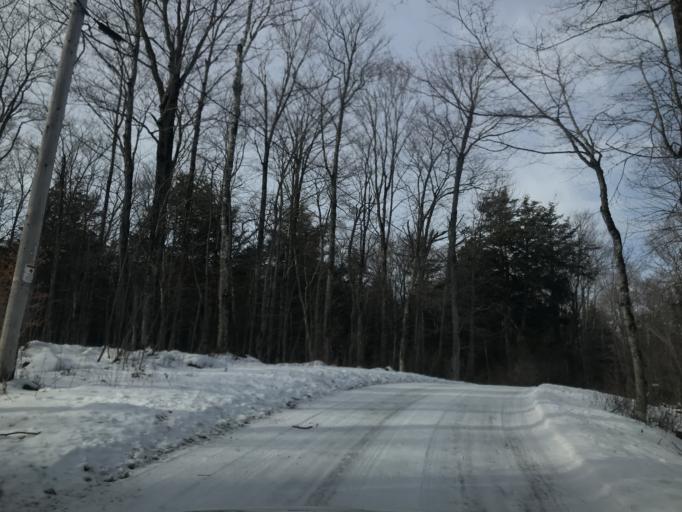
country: US
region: Wisconsin
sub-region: Door County
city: Sturgeon Bay
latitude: 45.1527
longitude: -87.0417
